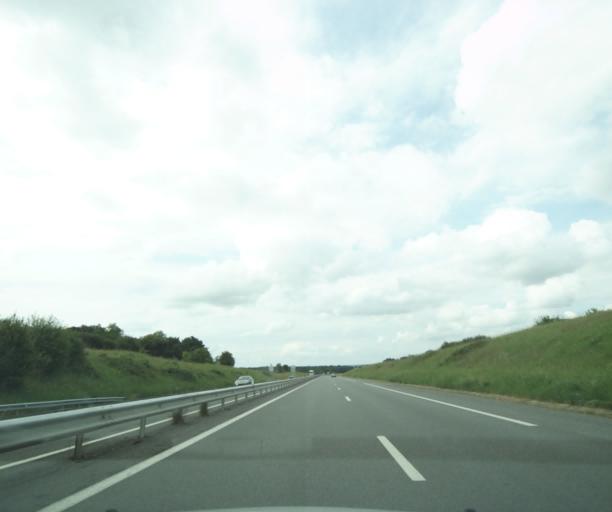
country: FR
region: Centre
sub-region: Departement du Cher
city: Orval
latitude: 46.7623
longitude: 2.4081
